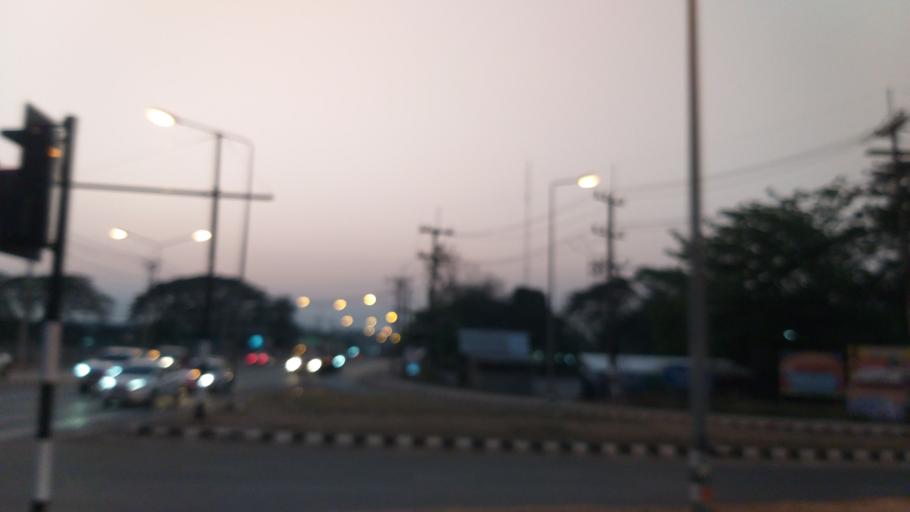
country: TH
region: Changwat Udon Thani
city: Nong Han
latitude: 17.3621
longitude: 103.1775
